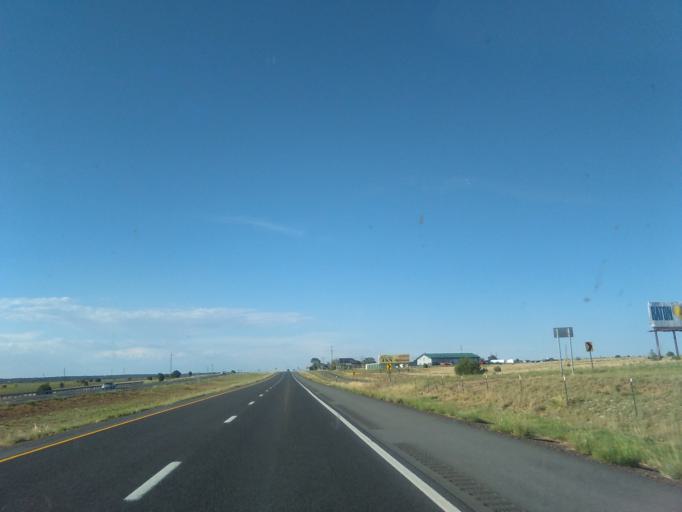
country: US
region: New Mexico
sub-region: San Miguel County
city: Las Vegas
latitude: 35.6528
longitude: -105.1908
